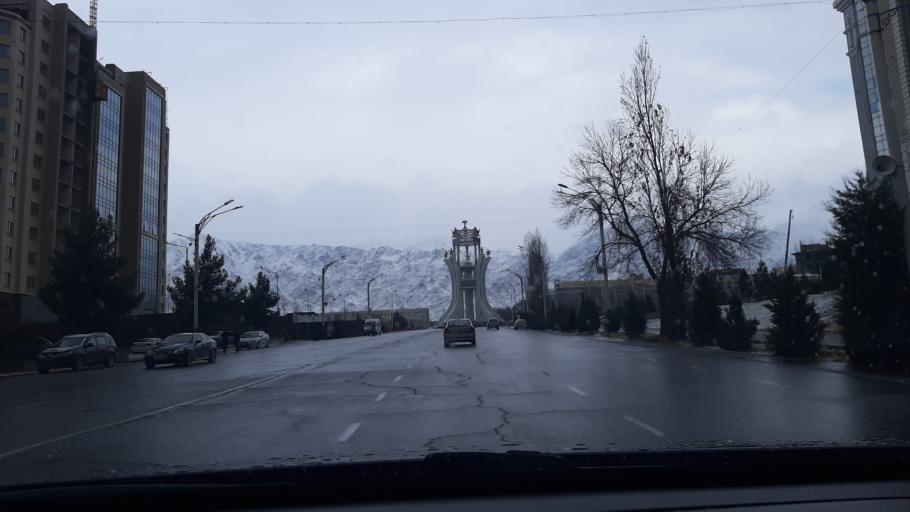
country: TJ
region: Viloyati Sughd
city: Khujand
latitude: 40.2991
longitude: 69.6149
